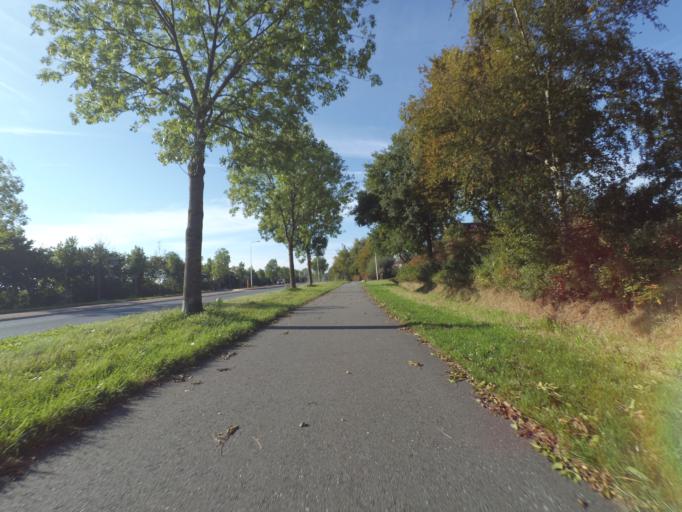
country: NL
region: Gelderland
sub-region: Gemeente Nijkerk
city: Nijkerk
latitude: 52.2104
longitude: 5.4994
